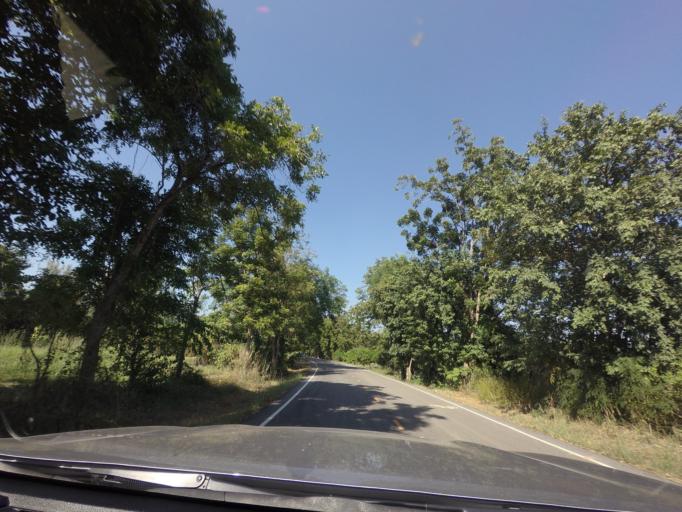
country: TH
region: Sukhothai
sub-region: Amphoe Si Satchanalai
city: Si Satchanalai
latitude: 17.4217
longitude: 99.7891
